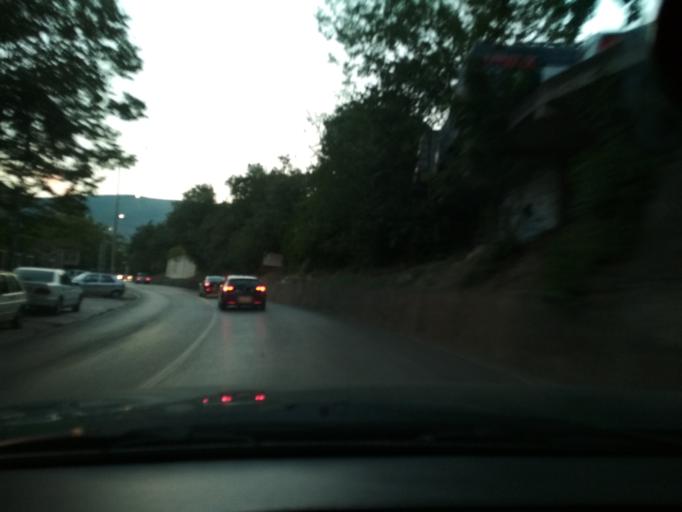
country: ME
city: Igalo
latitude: 42.4621
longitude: 18.5191
